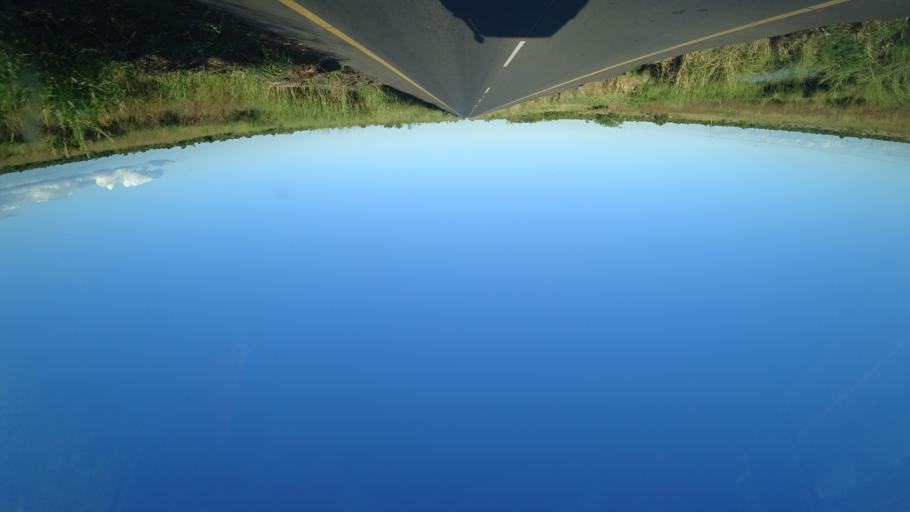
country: MZ
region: Sofala
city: Dondo
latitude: -19.3100
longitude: 34.2712
